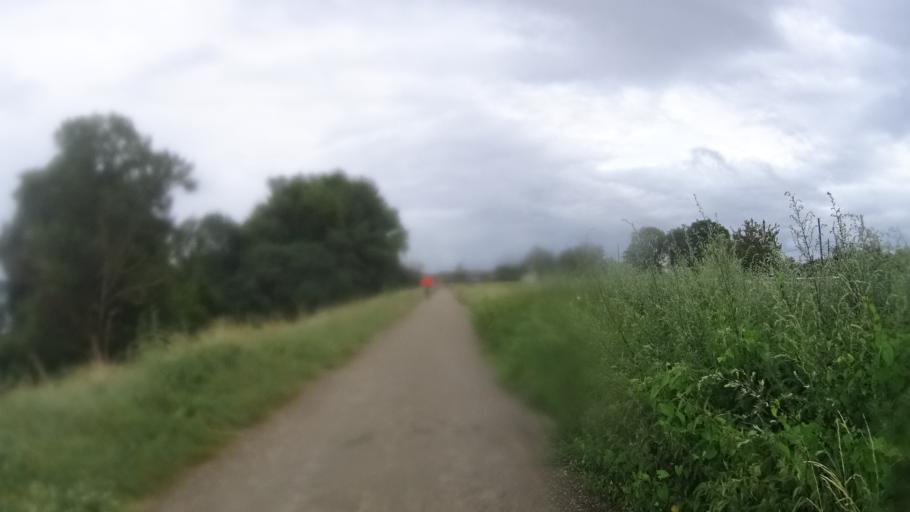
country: FR
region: Centre
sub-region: Departement du Loiret
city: Saint-Jean-le-Blanc
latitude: 47.8951
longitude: 1.9249
